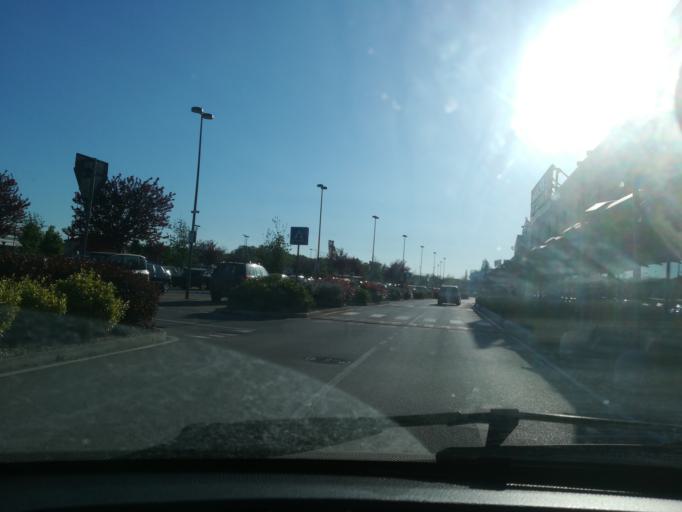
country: IT
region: The Marches
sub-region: Provincia di Macerata
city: Piediripa
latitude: 43.2699
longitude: 13.4816
